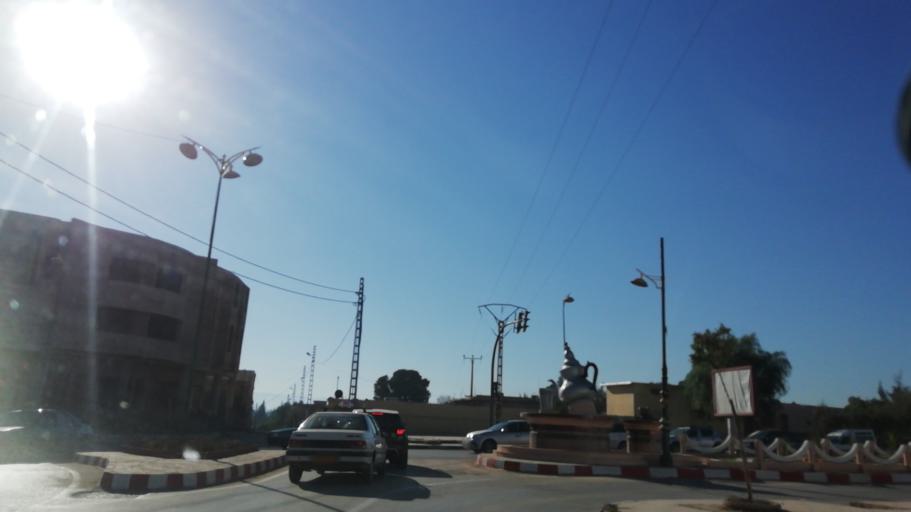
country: DZ
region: Tlemcen
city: Nedroma
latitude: 34.8462
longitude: -1.7396
